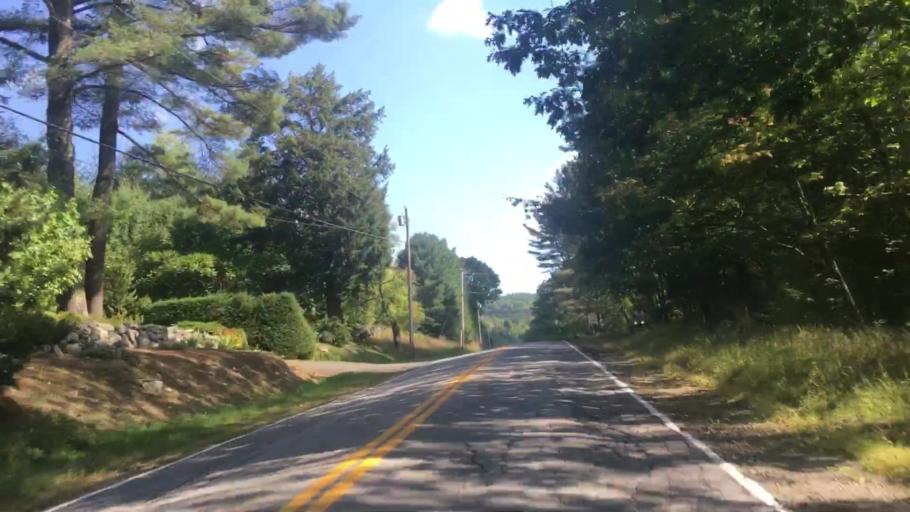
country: US
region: Maine
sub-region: Kennebec County
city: Mount Vernon
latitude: 44.5364
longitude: -69.9891
